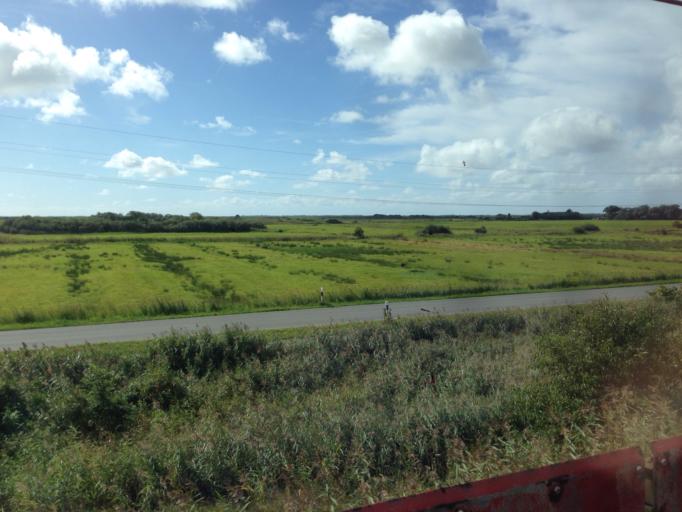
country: DE
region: Schleswig-Holstein
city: Keitum
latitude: 54.8847
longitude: 8.3800
